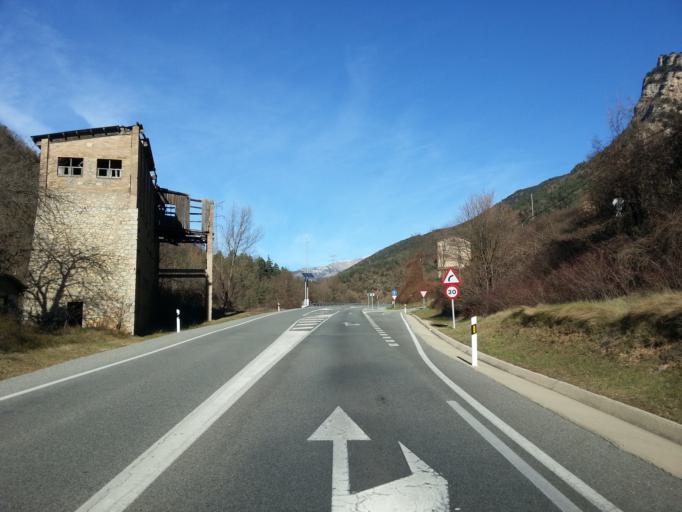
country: ES
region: Catalonia
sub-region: Provincia de Barcelona
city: Sant Julia de Cerdanyola
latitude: 42.1925
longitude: 1.8692
